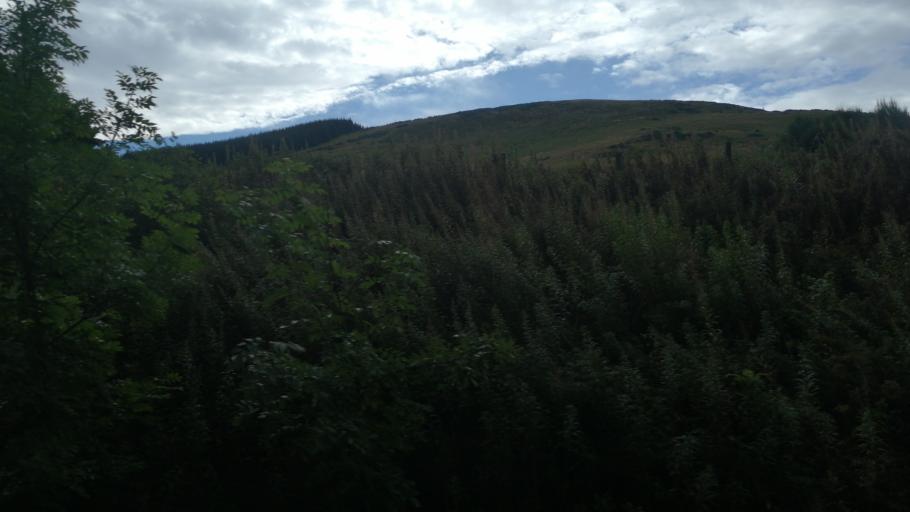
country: GB
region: Scotland
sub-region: Aberdeenshire
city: Insch
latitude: 57.3404
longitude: -2.6580
